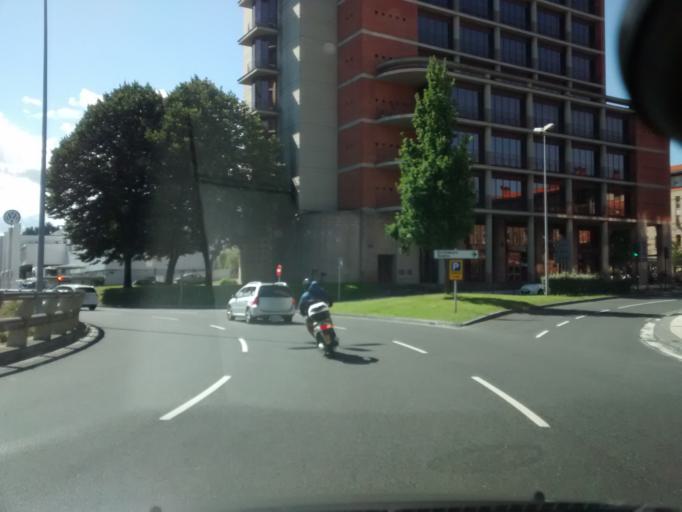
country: ES
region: Basque Country
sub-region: Provincia de Guipuzcoa
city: San Sebastian
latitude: 43.3016
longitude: -2.0035
